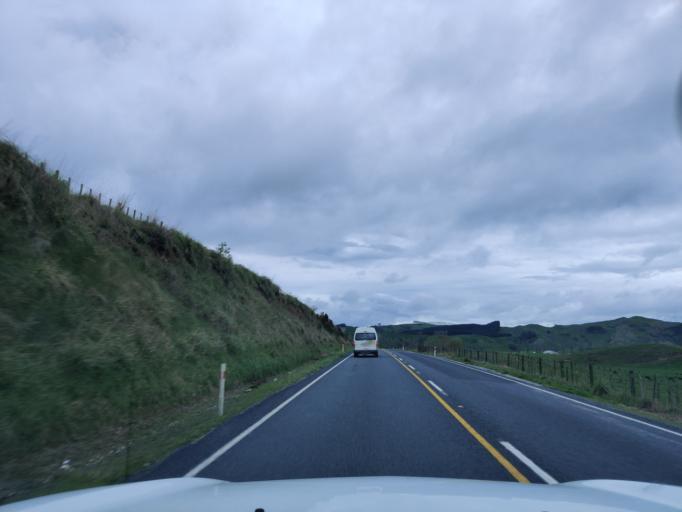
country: NZ
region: Waikato
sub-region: Otorohanga District
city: Otorohanga
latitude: -38.4603
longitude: 175.1678
